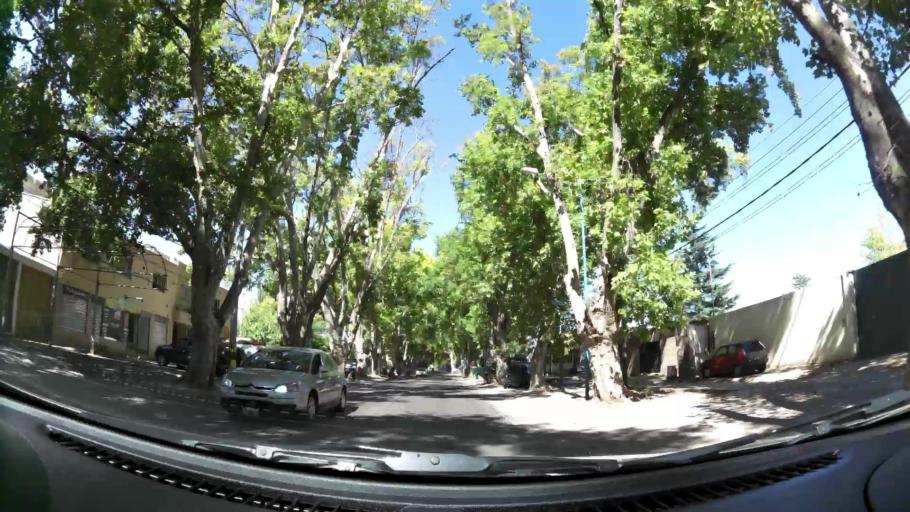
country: AR
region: Mendoza
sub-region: Departamento de Godoy Cruz
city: Godoy Cruz
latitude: -32.9502
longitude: -68.8448
